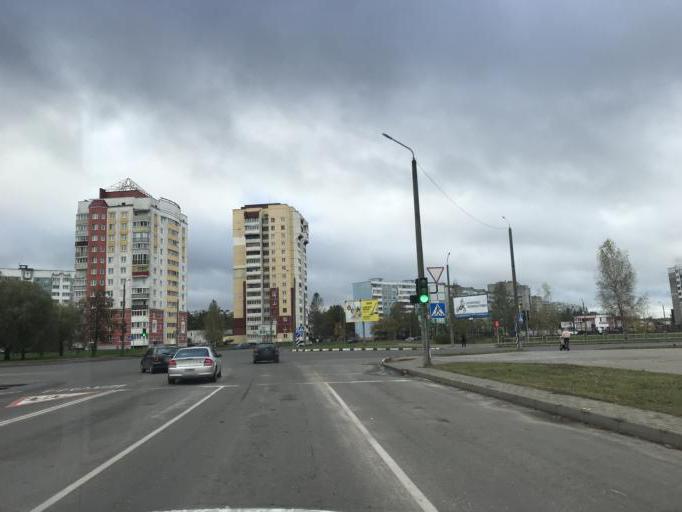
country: BY
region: Mogilev
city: Mahilyow
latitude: 53.8803
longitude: 30.3688
